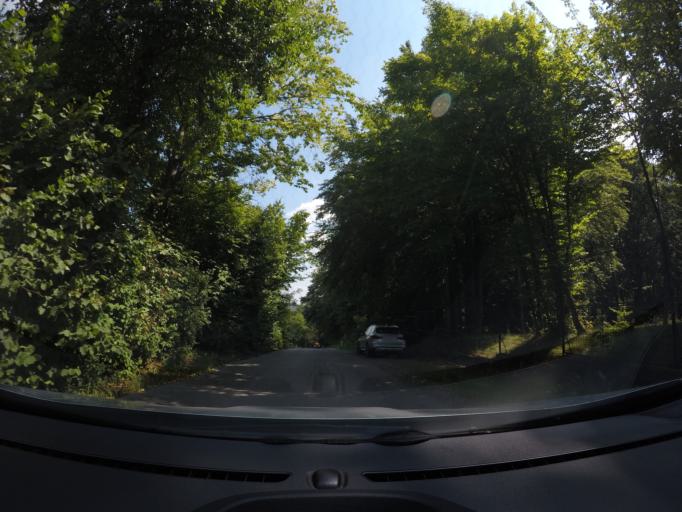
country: AT
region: Lower Austria
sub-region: Politischer Bezirk Wien-Umgebung
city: Mauerbach
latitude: 48.2701
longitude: 16.1599
